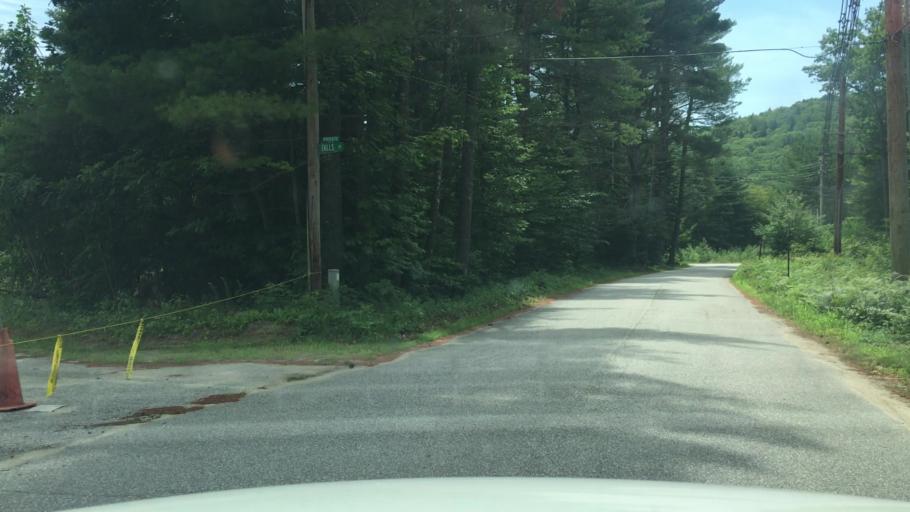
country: US
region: New Hampshire
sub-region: Grafton County
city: Plymouth
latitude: 43.7820
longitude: -71.6654
